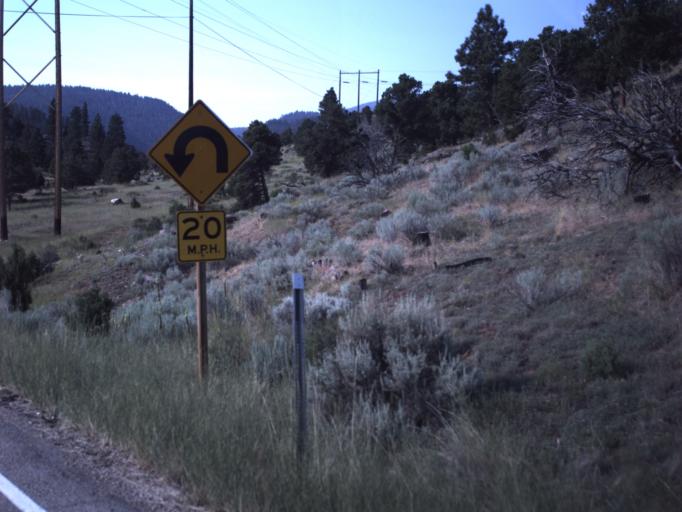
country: US
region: Utah
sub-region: Daggett County
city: Manila
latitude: 40.8955
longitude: -109.4472
